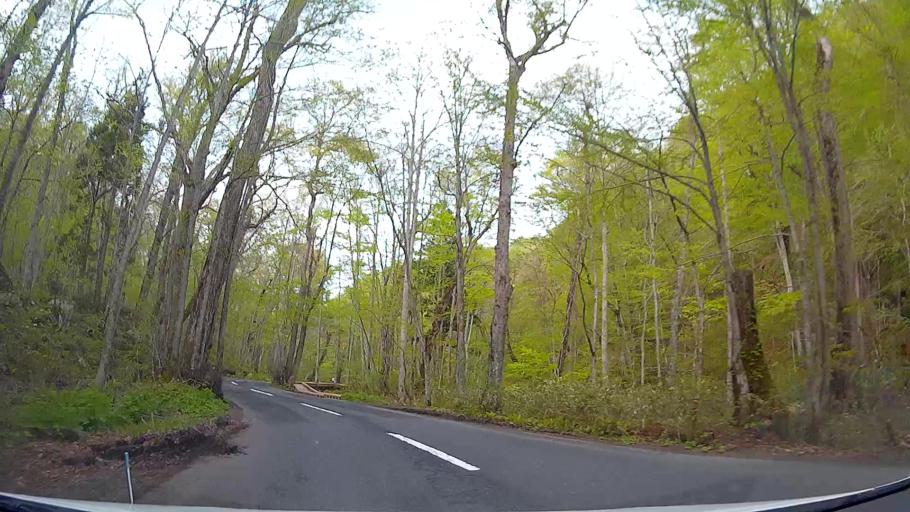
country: JP
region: Aomori
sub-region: Aomori Shi
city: Furudate
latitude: 40.5233
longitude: 140.9736
